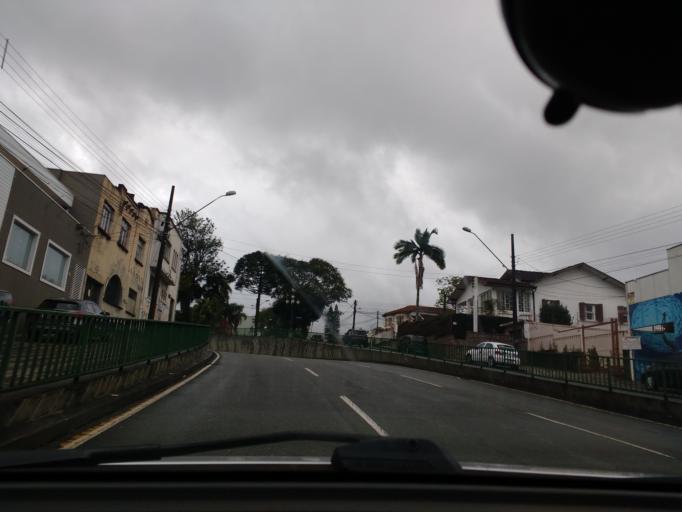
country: BR
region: Parana
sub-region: Curitiba
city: Curitiba
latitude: -25.4228
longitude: -49.2798
